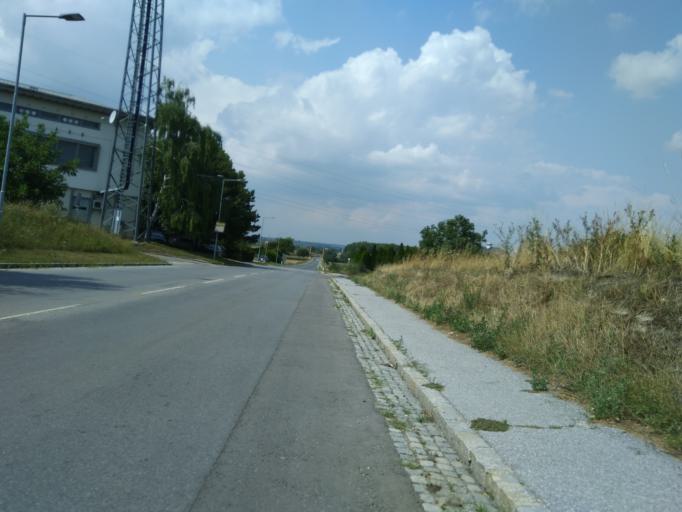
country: AT
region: Lower Austria
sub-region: Politischer Bezirk Ganserndorf
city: Ganserndorf
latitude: 48.3438
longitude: 16.7144
